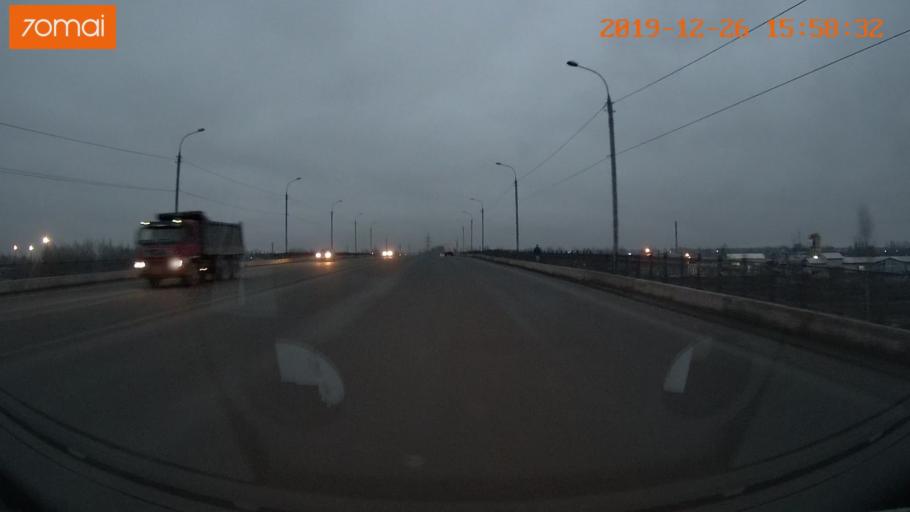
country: RU
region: Jaroslavl
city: Rybinsk
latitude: 58.0383
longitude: 38.7963
